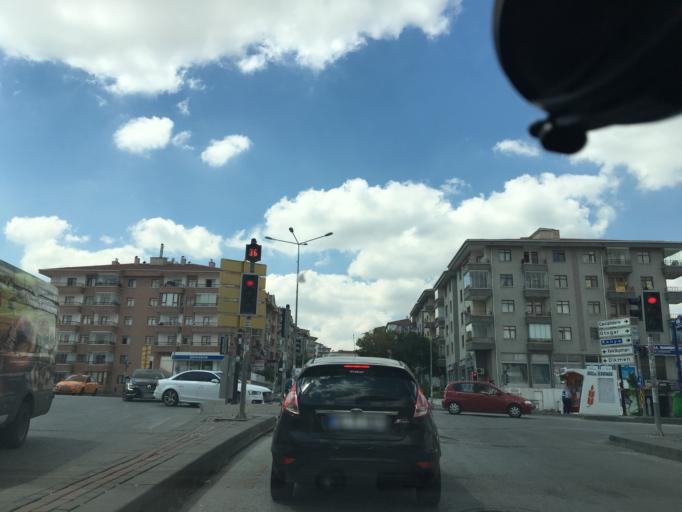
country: TR
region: Ankara
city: Ankara
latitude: 39.8851
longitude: 32.8287
